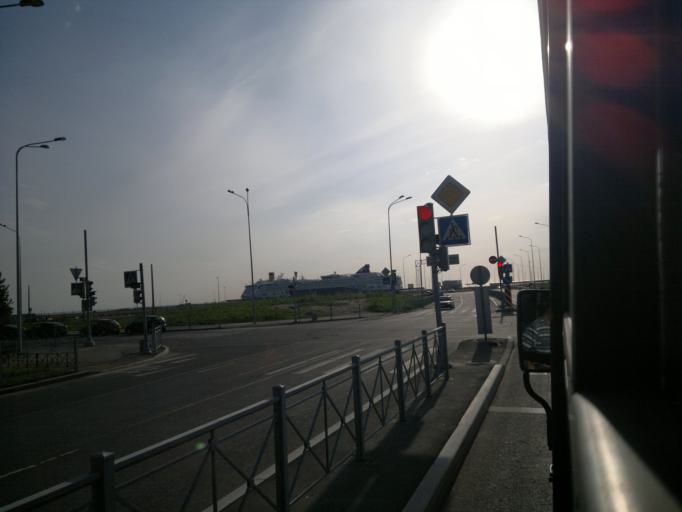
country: RU
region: St.-Petersburg
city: Vasyl'evsky Ostrov
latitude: 59.9503
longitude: 30.2178
